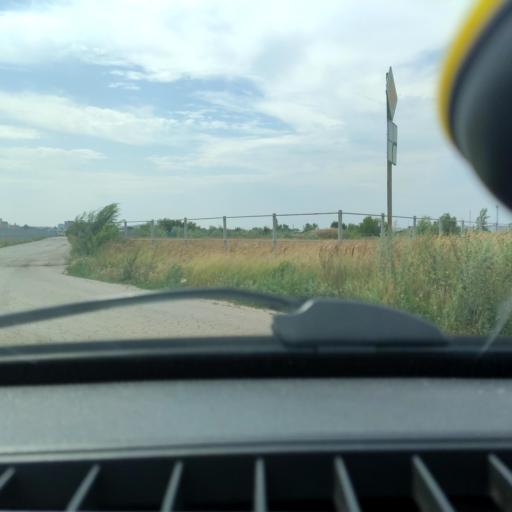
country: RU
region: Samara
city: Tol'yatti
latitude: 53.5609
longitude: 49.3442
